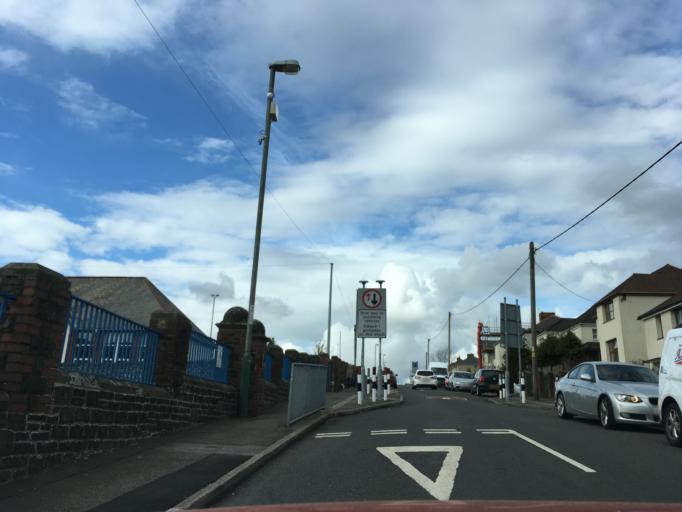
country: GB
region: Wales
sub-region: Caerphilly County Borough
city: Rhymney
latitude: 51.7423
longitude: -3.2955
